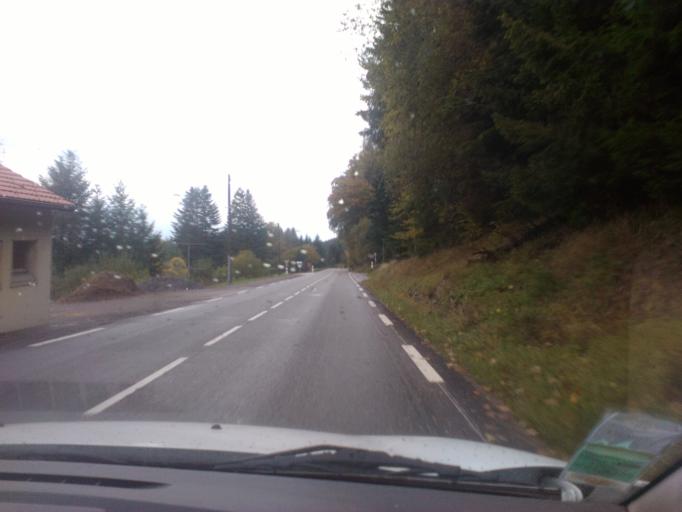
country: FR
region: Lorraine
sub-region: Departement des Vosges
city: Xonrupt-Longemer
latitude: 48.1211
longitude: 6.9120
